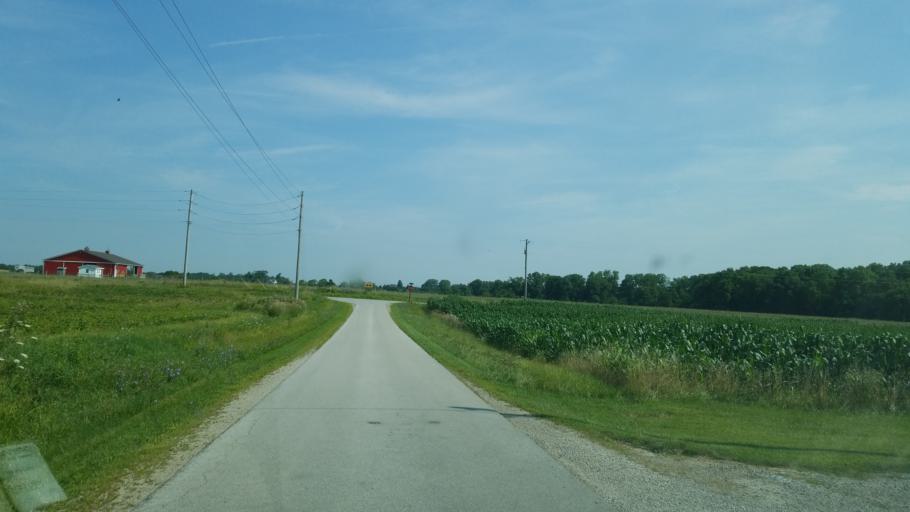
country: US
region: Ohio
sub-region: Sandusky County
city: Green Springs
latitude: 41.1384
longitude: -82.9960
